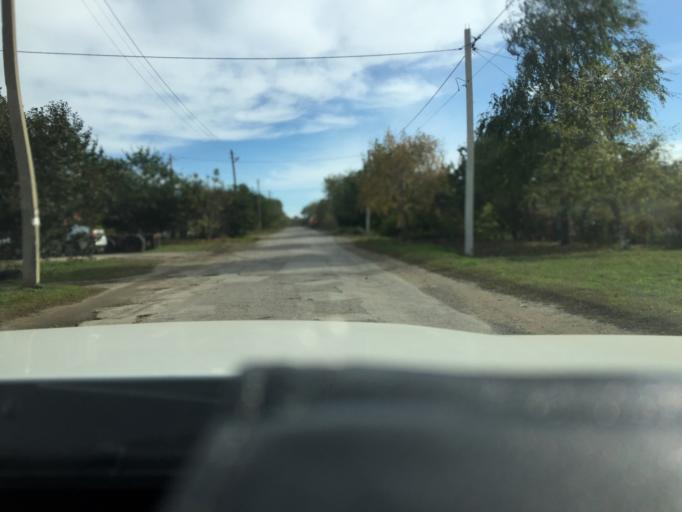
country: RU
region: Rostov
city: Aksay
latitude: 47.3040
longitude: 39.8300
